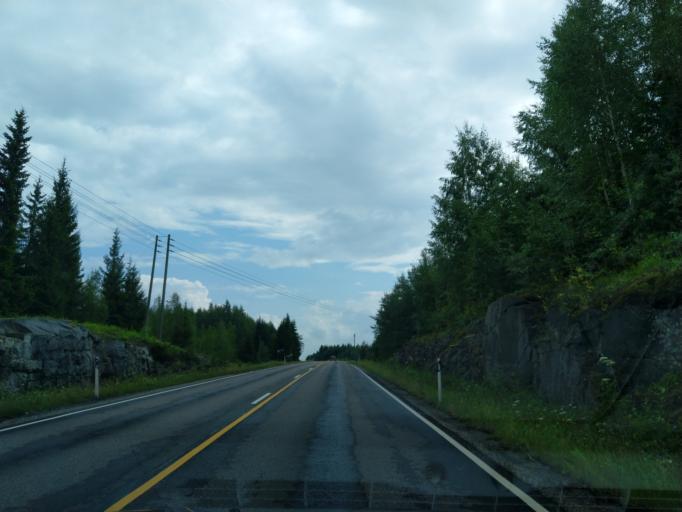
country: FI
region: South Karelia
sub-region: Imatra
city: Parikkala
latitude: 61.6184
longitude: 29.4441
